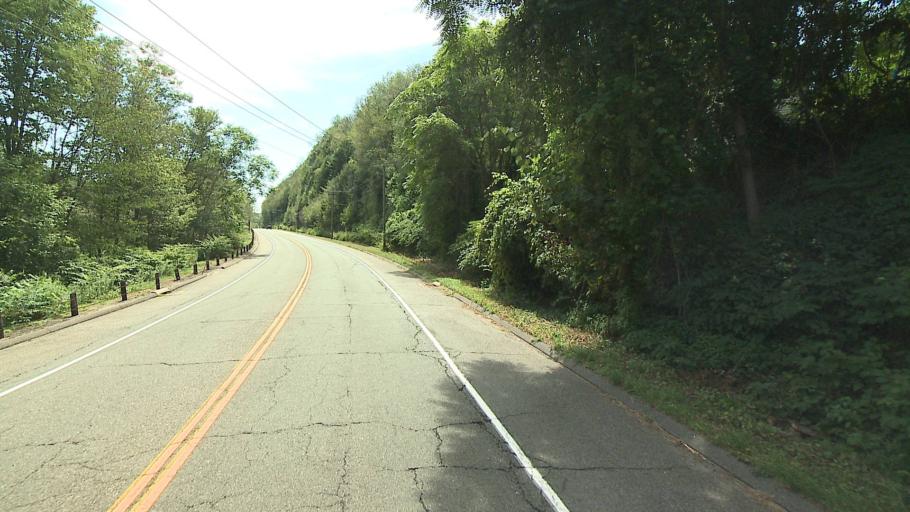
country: US
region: Connecticut
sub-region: Hartford County
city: Collinsville
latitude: 41.8020
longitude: -72.9286
